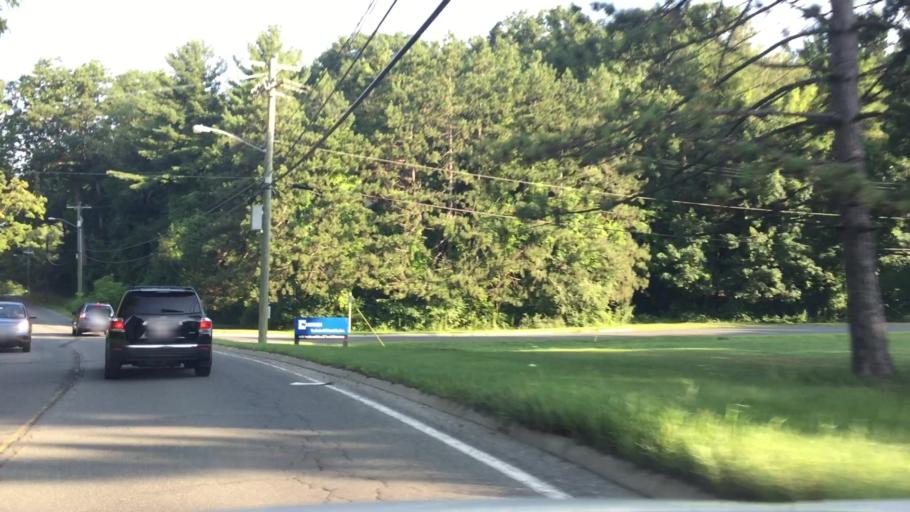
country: US
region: Massachusetts
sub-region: Berkshire County
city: Dalton
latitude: 42.4629
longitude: -73.1893
